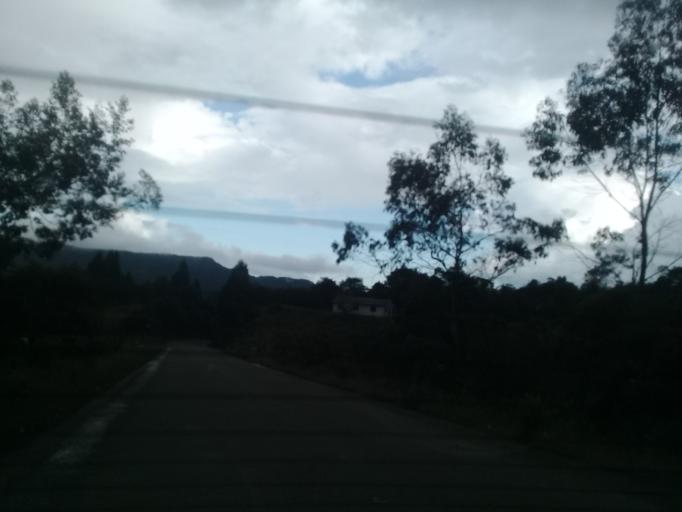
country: CO
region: Cundinamarca
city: Junin
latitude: 4.8515
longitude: -73.7444
